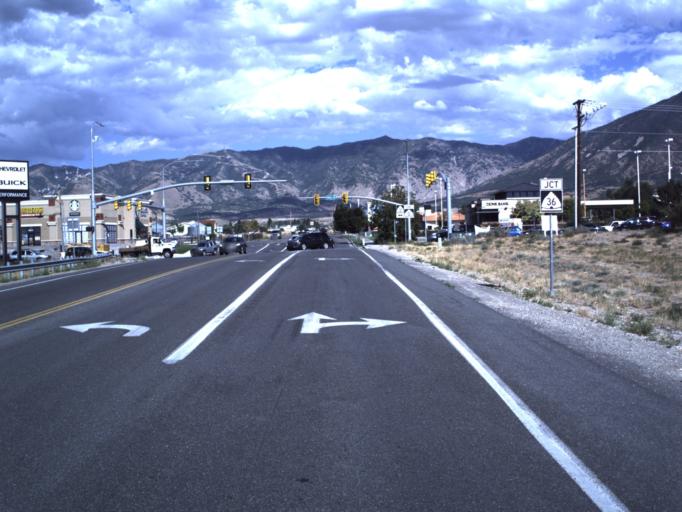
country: US
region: Utah
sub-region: Tooele County
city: Tooele
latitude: 40.5510
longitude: -112.2994
